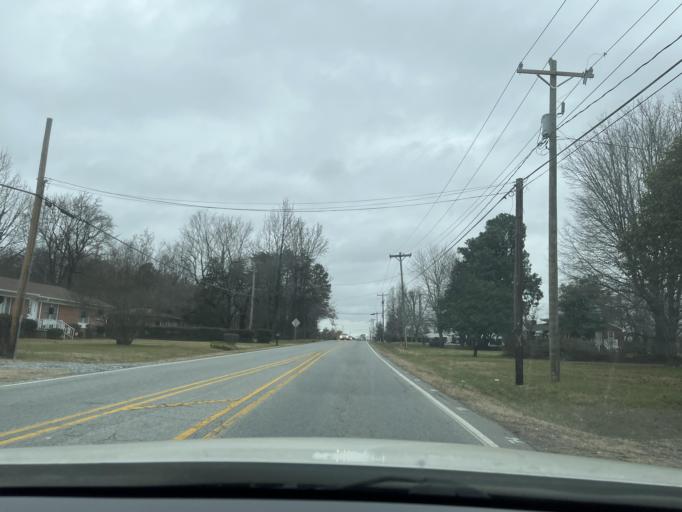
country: US
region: North Carolina
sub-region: Guilford County
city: Pleasant Garden
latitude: 35.9972
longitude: -79.8049
